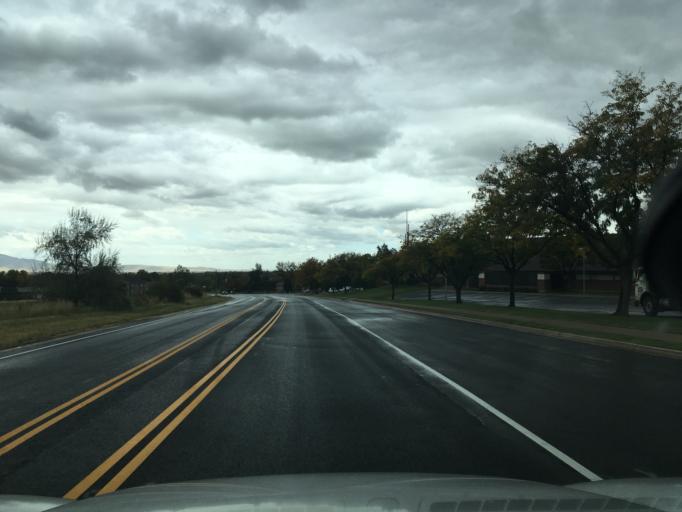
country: US
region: Utah
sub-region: Davis County
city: Kaysville
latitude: 41.0626
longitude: -111.9377
